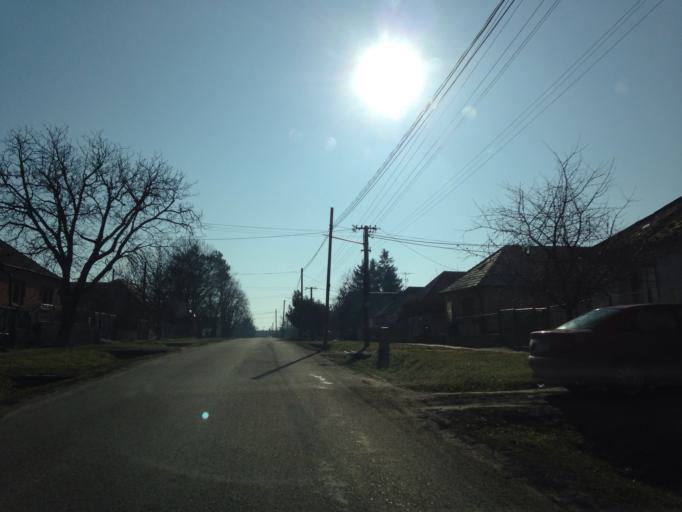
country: SK
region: Nitriansky
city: Svodin
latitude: 47.9284
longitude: 18.4001
